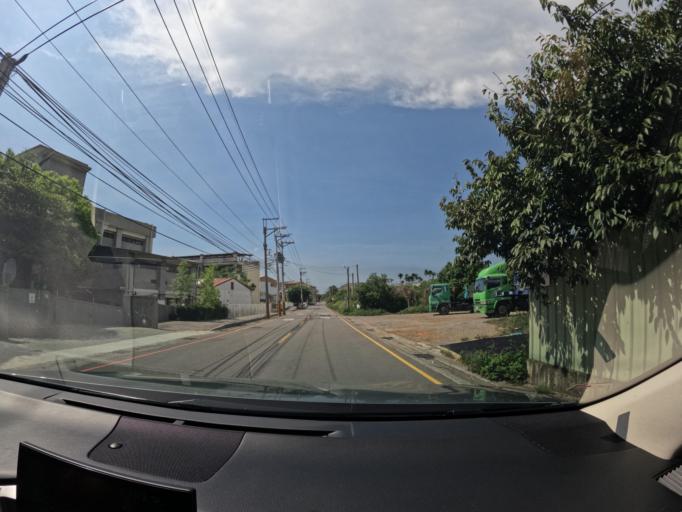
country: TW
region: Taiwan
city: Fengyuan
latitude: 24.3099
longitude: 120.7303
